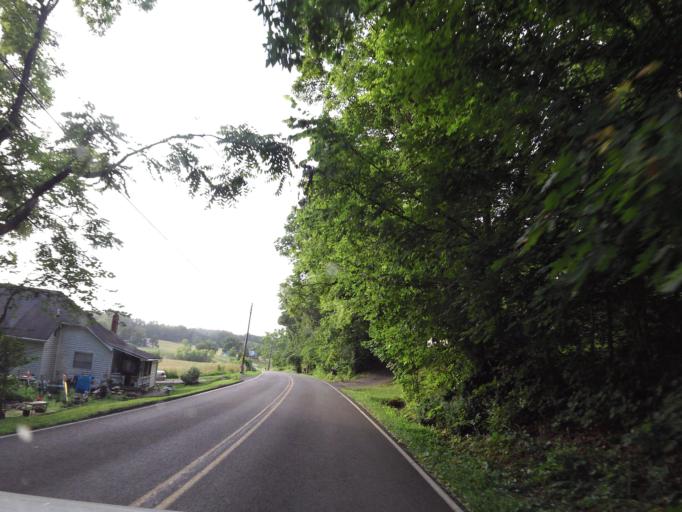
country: US
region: Tennessee
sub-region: Sevier County
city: Seymour
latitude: 35.9018
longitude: -83.8020
